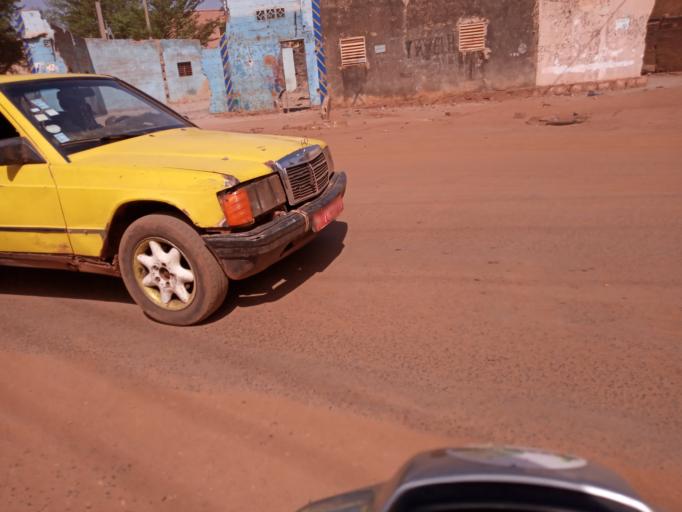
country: ML
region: Bamako
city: Bamako
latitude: 12.5878
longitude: -7.9581
